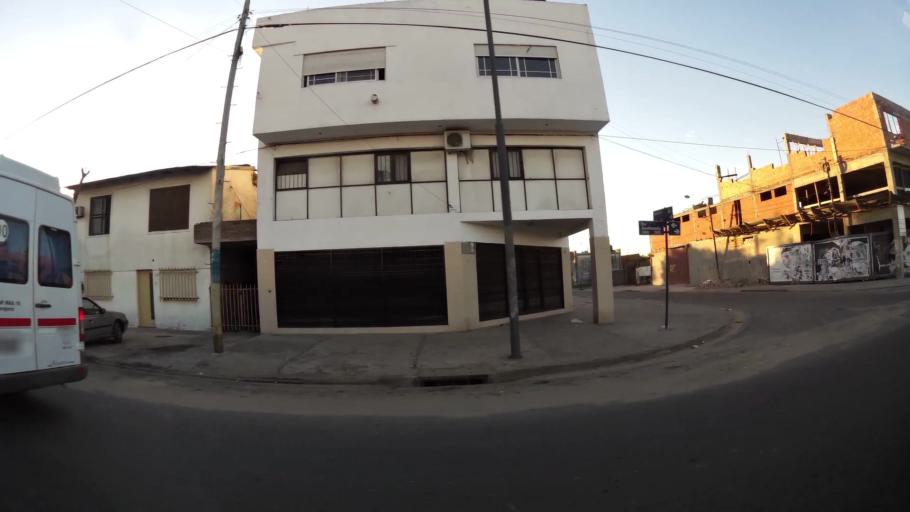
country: AR
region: Santa Fe
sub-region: Departamento de Rosario
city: Rosario
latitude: -32.9708
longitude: -60.6872
